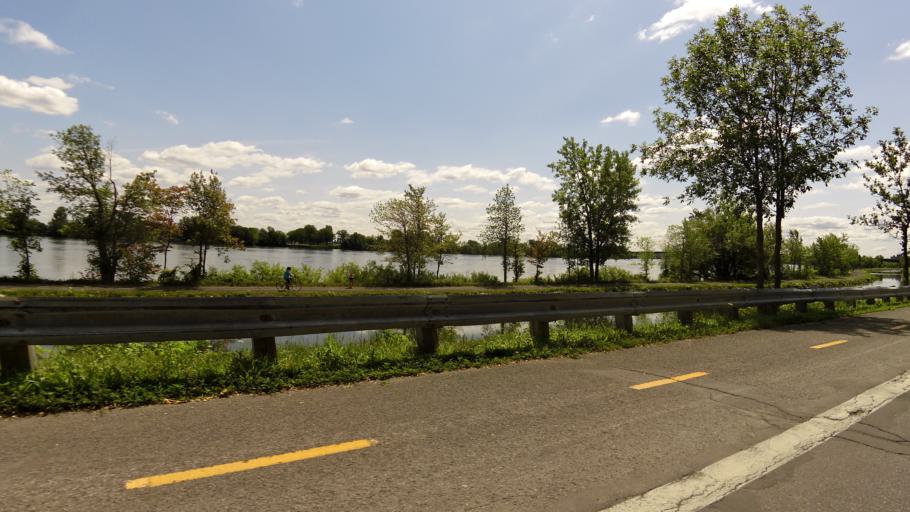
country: CA
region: Quebec
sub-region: Monteregie
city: Saint-Jean-sur-Richelieu
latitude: 45.3343
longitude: -73.2650
